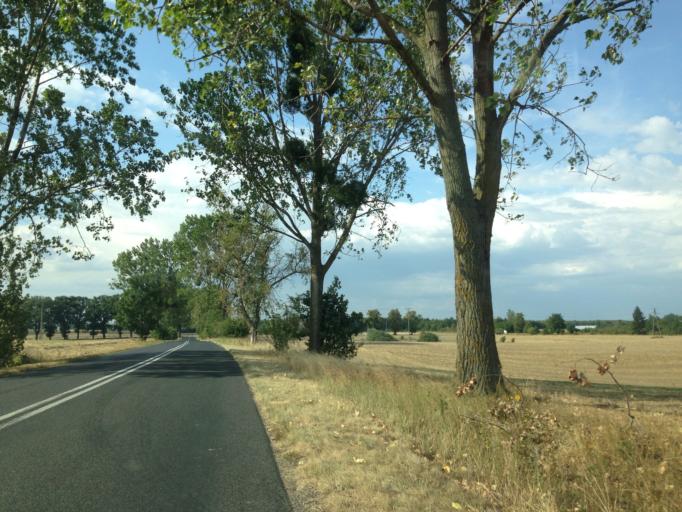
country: PL
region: Kujawsko-Pomorskie
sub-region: Powiat swiecki
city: Bukowiec
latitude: 53.3864
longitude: 18.2955
